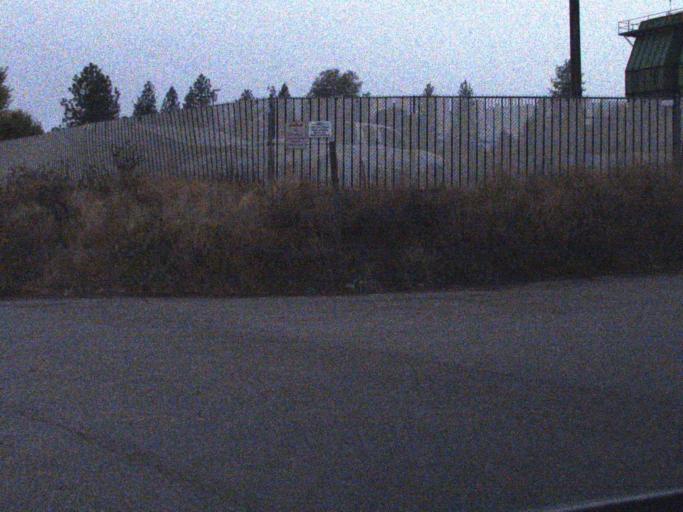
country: US
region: Washington
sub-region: Stevens County
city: Kettle Falls
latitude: 48.6086
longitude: -118.0688
